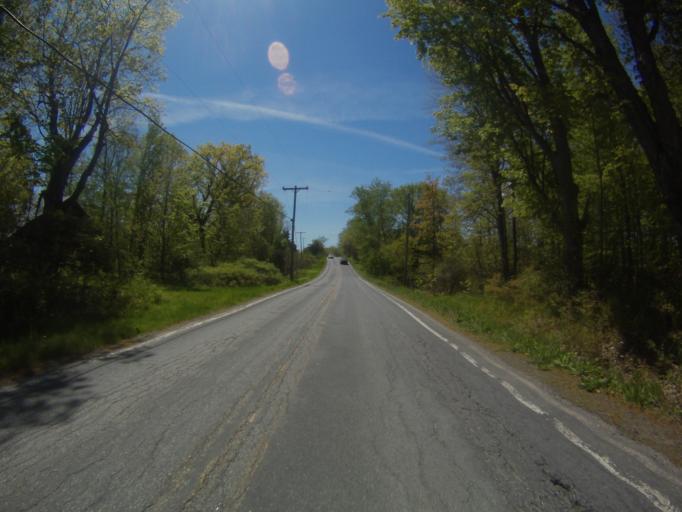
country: US
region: New York
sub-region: Essex County
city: Port Henry
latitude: 43.9743
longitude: -73.4224
